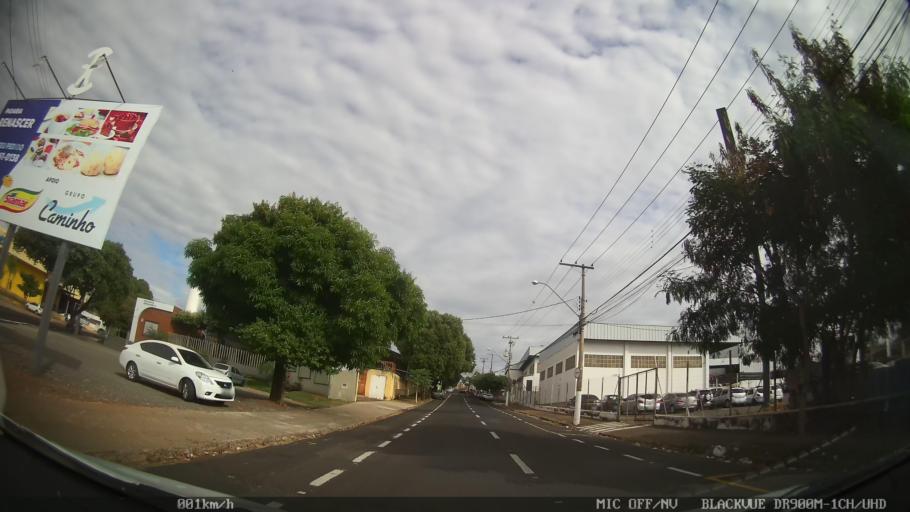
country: BR
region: Sao Paulo
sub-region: Sao Jose Do Rio Preto
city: Sao Jose do Rio Preto
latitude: -20.8266
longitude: -49.4045
